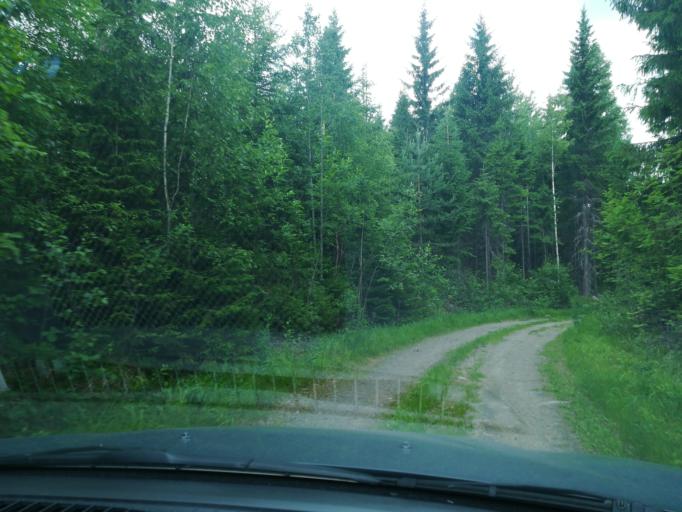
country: FI
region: Southern Savonia
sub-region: Mikkeli
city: Mikkeli
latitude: 61.6736
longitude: 27.1139
